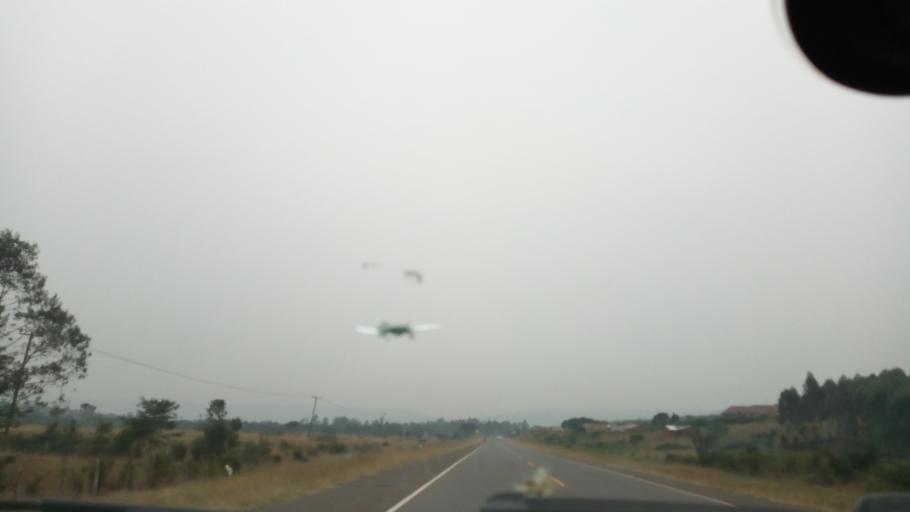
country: UG
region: Western Region
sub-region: Mbarara District
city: Mbarara
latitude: -0.7252
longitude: 30.7301
